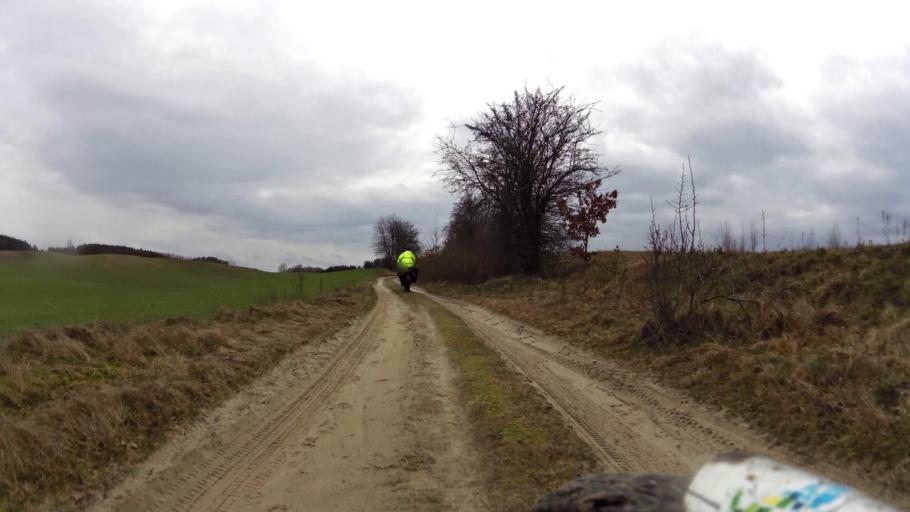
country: PL
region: Pomeranian Voivodeship
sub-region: Powiat bytowski
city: Miastko
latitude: 54.0179
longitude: 17.0071
